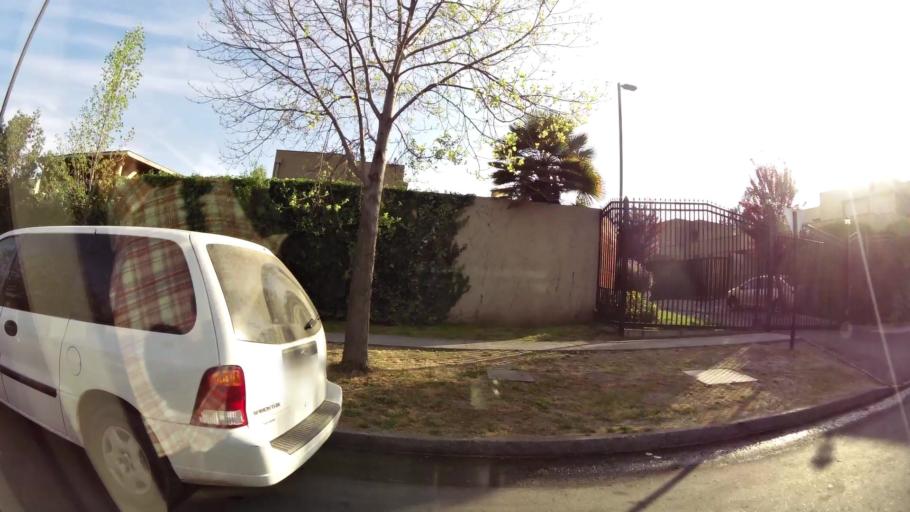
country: CL
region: Santiago Metropolitan
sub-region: Provincia de Cordillera
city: Puente Alto
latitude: -33.5582
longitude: -70.5486
